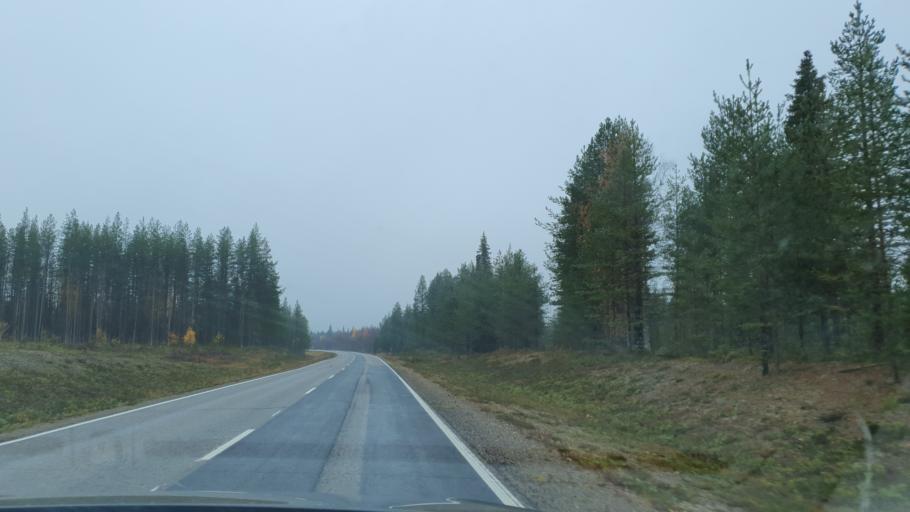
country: FI
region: Lapland
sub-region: Tunturi-Lappi
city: Kittilae
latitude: 67.4020
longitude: 24.9169
